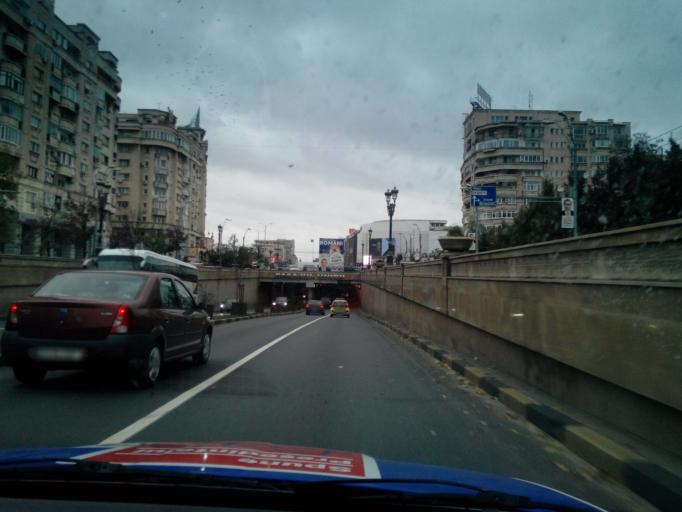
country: RO
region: Bucuresti
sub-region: Municipiul Bucuresti
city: Bucharest
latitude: 44.4239
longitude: 26.1043
